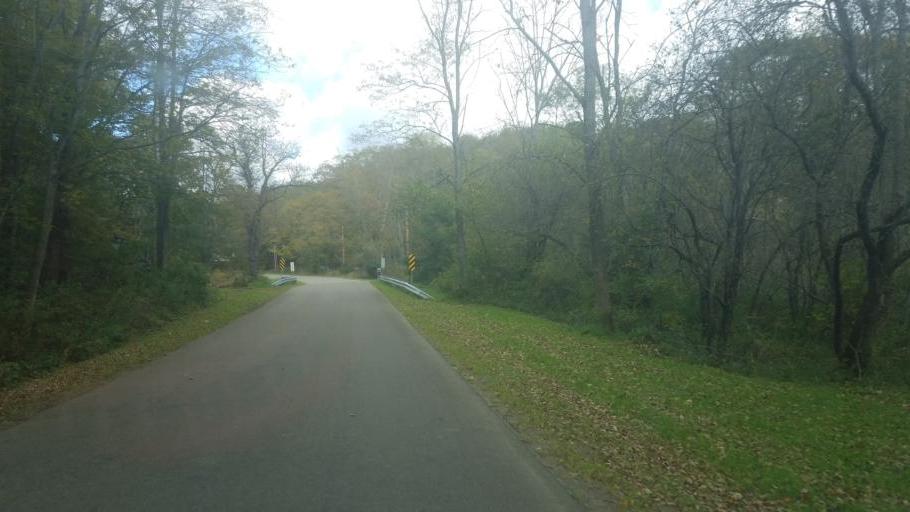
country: US
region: New York
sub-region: Cattaraugus County
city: Weston Mills
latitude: 42.1460
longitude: -78.3520
